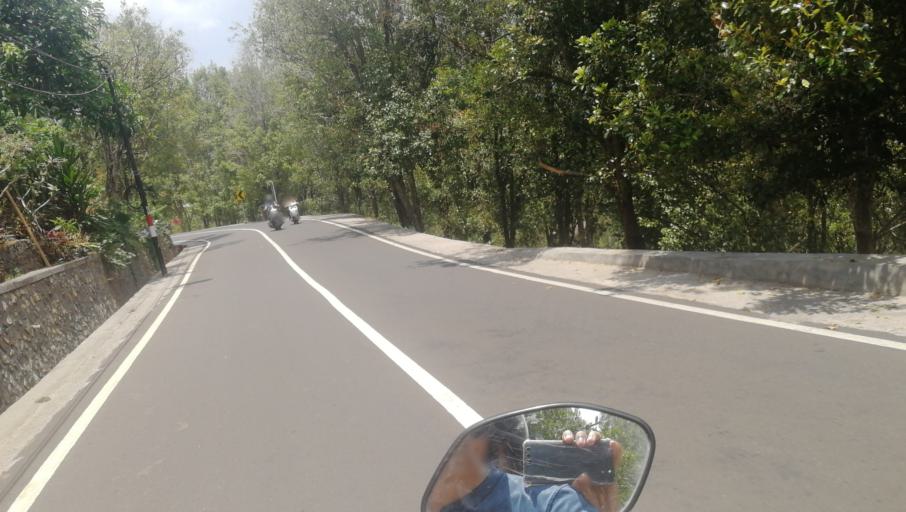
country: ID
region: Bali
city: Banjar Pedawa
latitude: -8.2634
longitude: 115.0420
